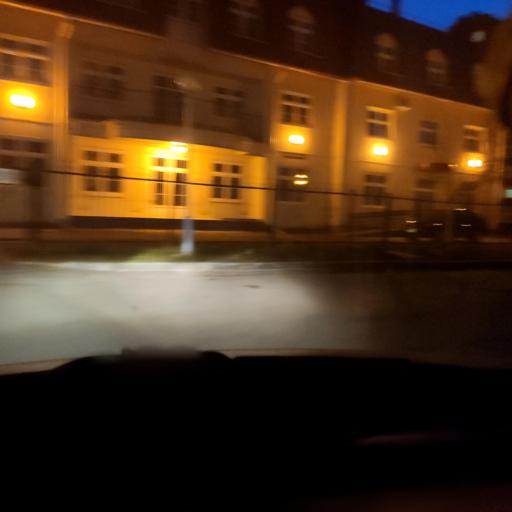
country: RU
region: Samara
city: Tol'yatti
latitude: 53.5405
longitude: 49.3354
